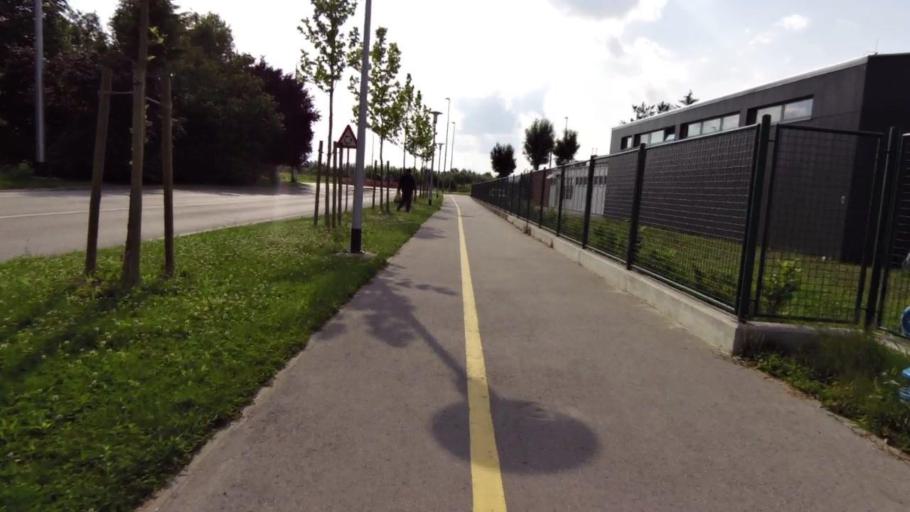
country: HR
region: Grad Zagreb
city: Stenjevec
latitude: 45.8043
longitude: 15.8761
